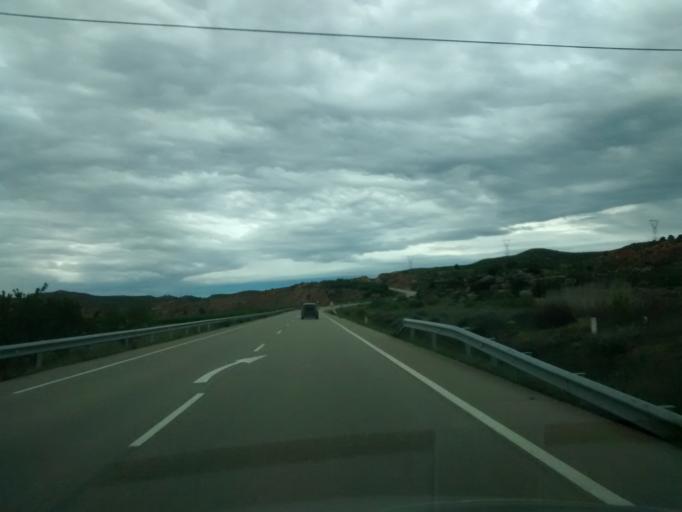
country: ES
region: Aragon
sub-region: Provincia de Zaragoza
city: Caspe
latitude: 41.1960
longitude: 0.0436
